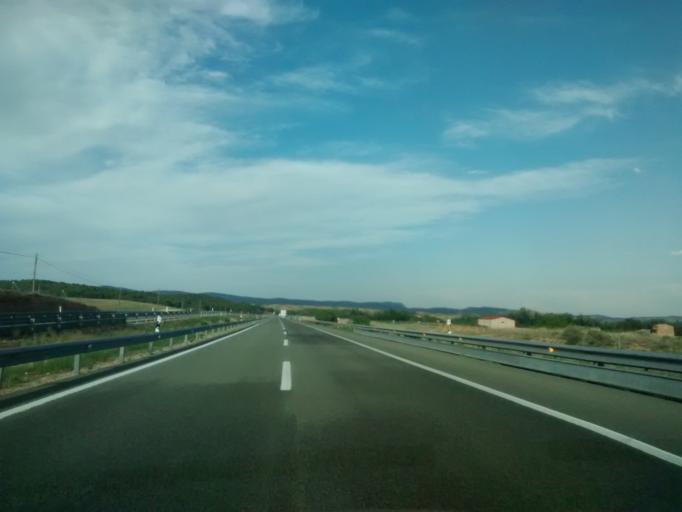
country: ES
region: Aragon
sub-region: Provincia de Zaragoza
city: Ariza
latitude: 41.3153
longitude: -2.0362
